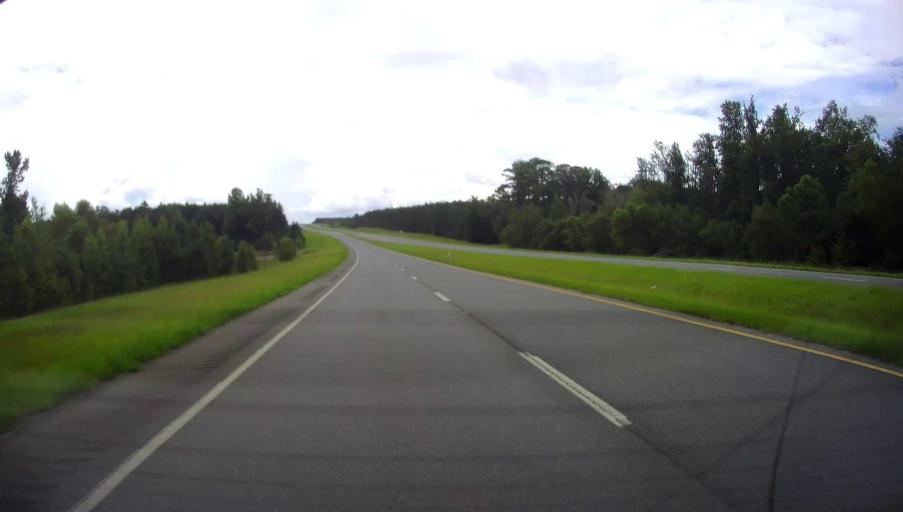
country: US
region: Georgia
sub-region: Schley County
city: Ellaville
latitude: 32.2724
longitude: -84.2996
